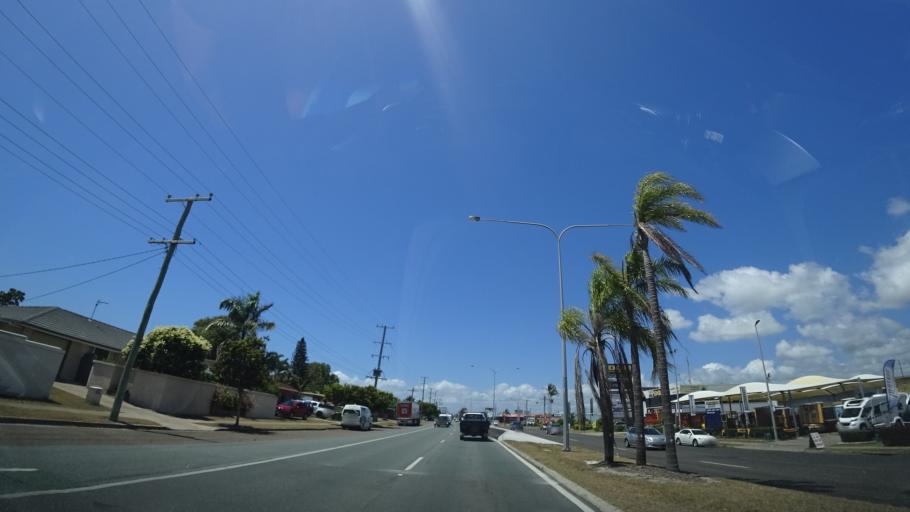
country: AU
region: Queensland
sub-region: Sunshine Coast
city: Mooloolaba
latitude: -26.7260
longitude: 153.1294
